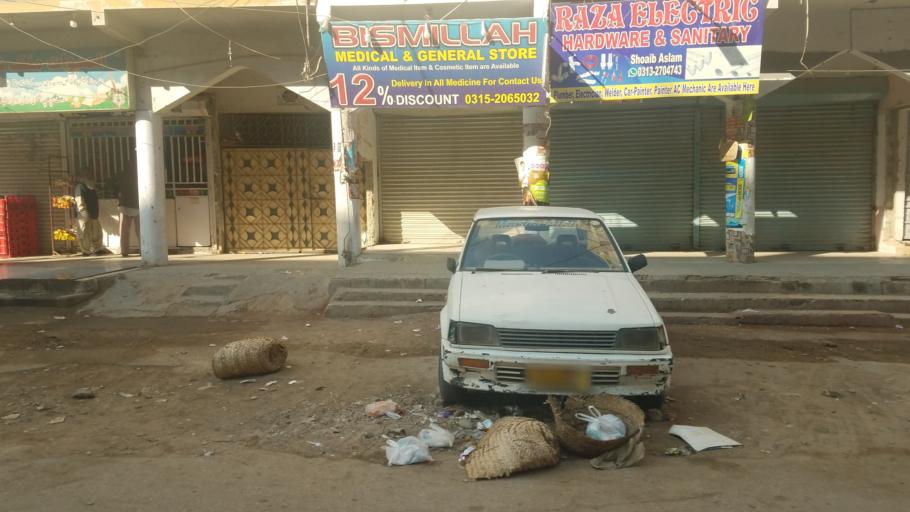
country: PK
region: Sindh
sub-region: Karachi District
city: Karachi
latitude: 24.9374
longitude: 67.0658
